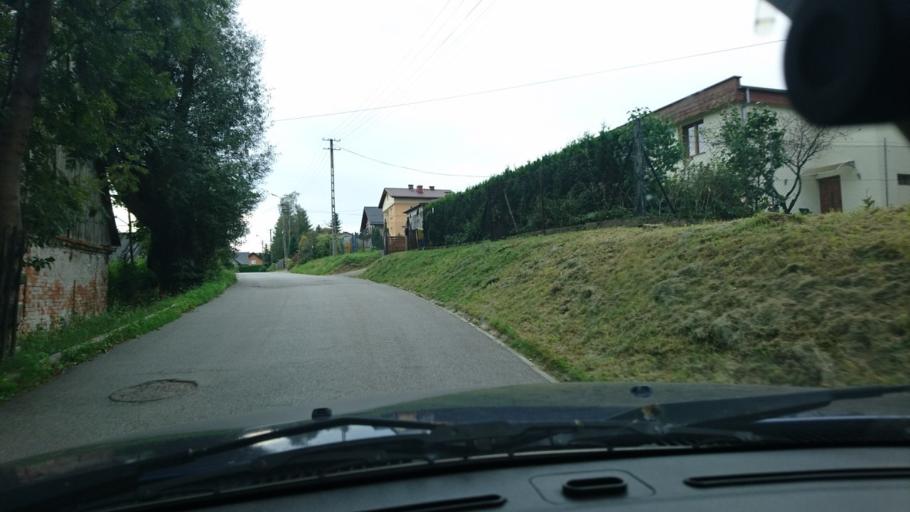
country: PL
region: Silesian Voivodeship
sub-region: Powiat bielski
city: Mazancowice
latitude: 49.8251
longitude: 19.0026
